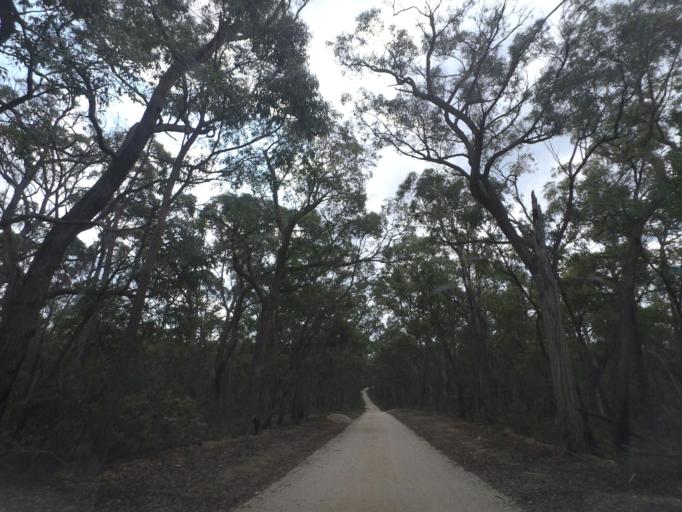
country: AU
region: Victoria
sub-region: Moorabool
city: Bacchus Marsh
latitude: -37.5096
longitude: 144.4295
